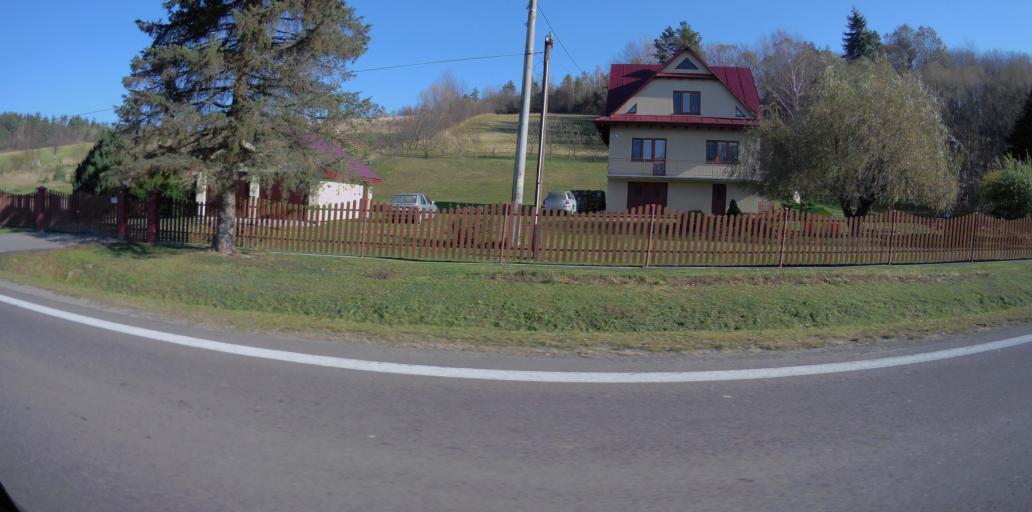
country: PL
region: Subcarpathian Voivodeship
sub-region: Powiat bieszczadzki
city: Ustrzyki Dolne
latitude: 49.5381
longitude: 22.5948
